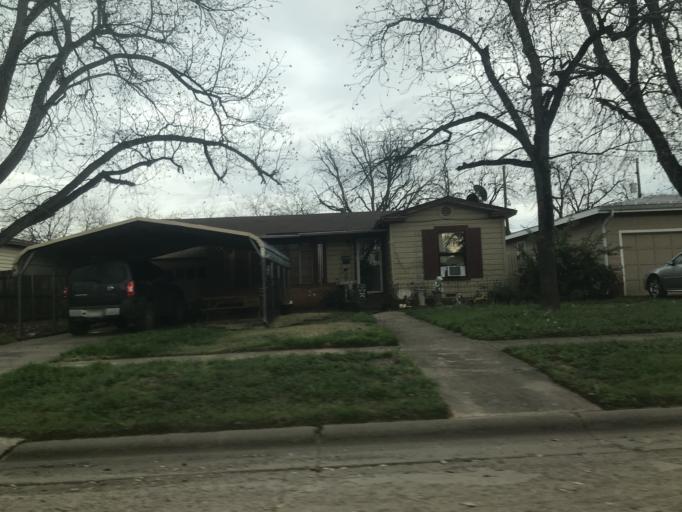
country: US
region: Texas
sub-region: Taylor County
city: Abilene
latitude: 32.4619
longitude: -99.7557
